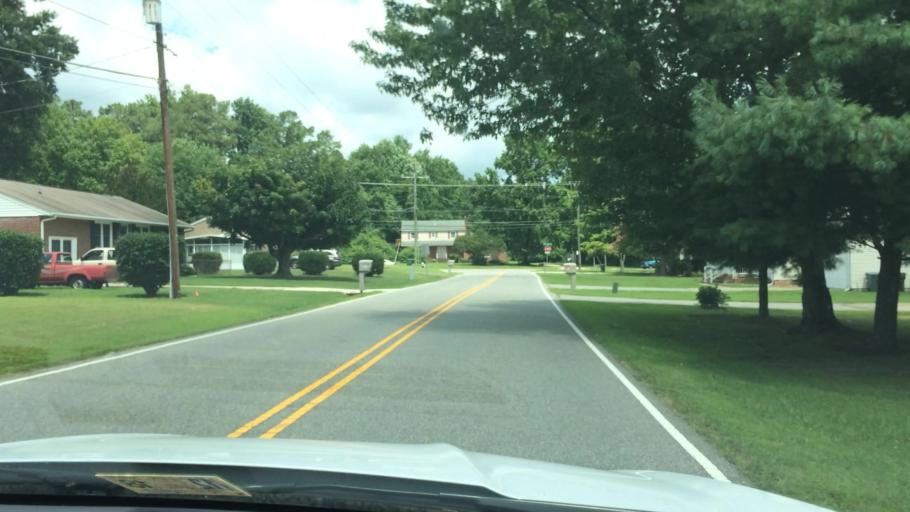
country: US
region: Virginia
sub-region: York County
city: Yorktown
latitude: 37.1503
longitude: -76.4502
